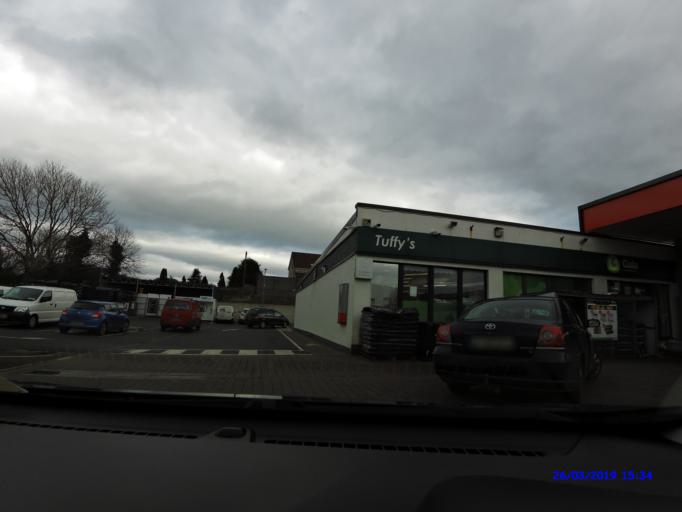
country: IE
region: Connaught
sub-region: Maigh Eo
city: Ballina
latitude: 54.1061
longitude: -9.1632
